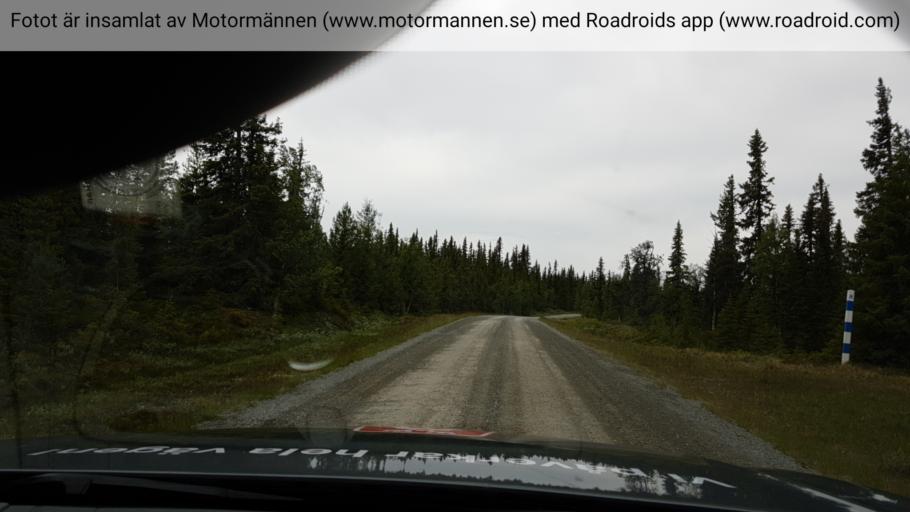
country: SE
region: Jaemtland
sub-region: Bergs Kommun
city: Hoverberg
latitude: 62.8527
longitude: 13.8853
